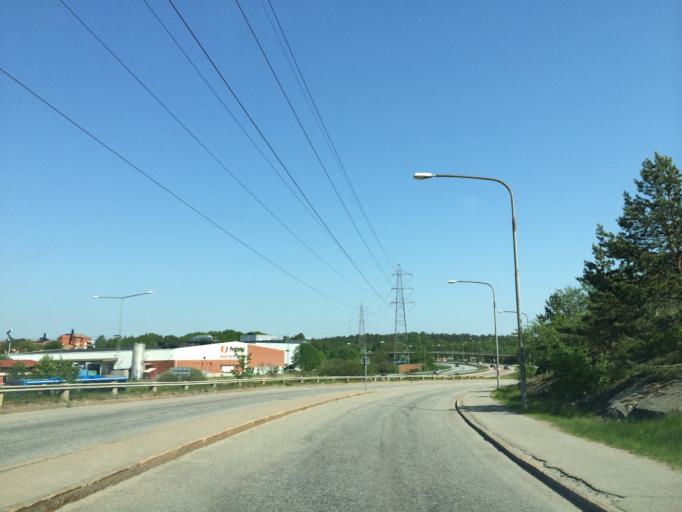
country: SE
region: Stockholm
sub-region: Nacka Kommun
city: Alta
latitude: 59.2624
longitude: 18.1277
